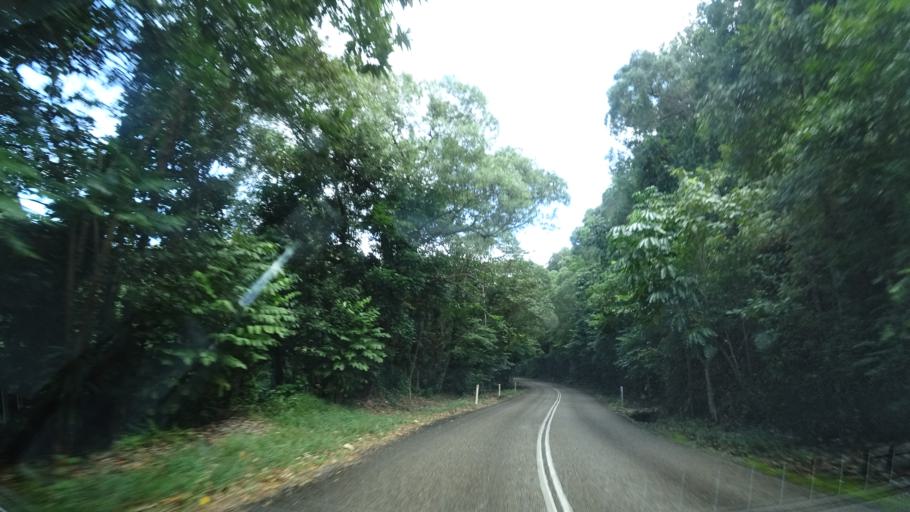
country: AU
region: Queensland
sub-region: Cairns
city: Port Douglas
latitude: -16.2471
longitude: 145.4346
